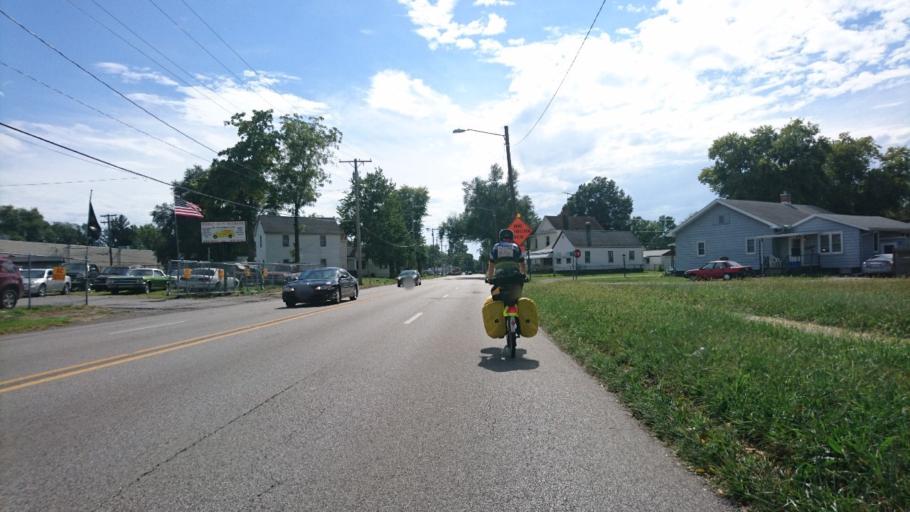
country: US
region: Illinois
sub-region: Sangamon County
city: Springfield
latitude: 39.8251
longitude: -89.6415
